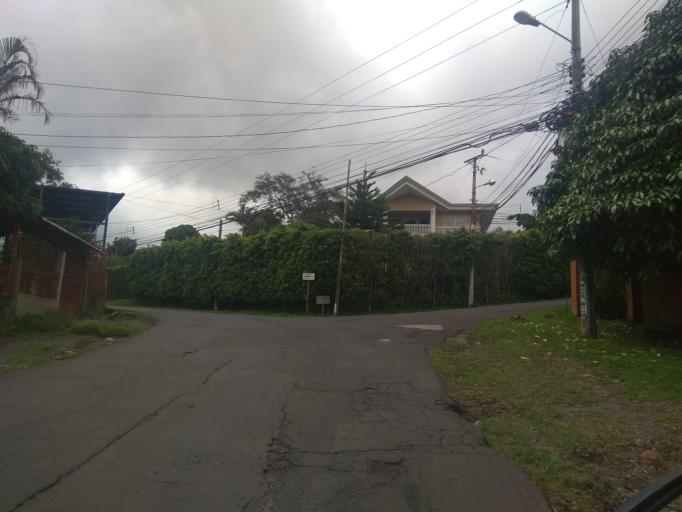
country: CR
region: Heredia
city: San Josecito
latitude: 10.0295
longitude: -84.1073
